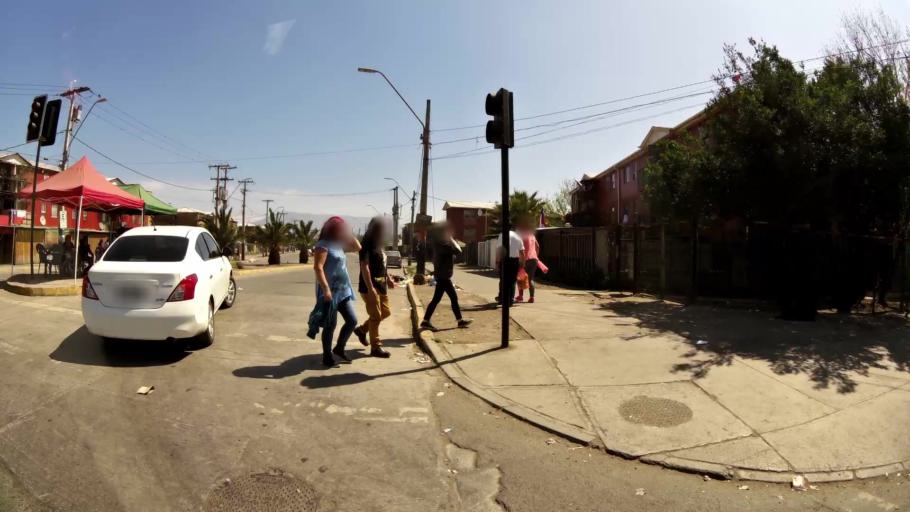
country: CL
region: Santiago Metropolitan
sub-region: Provincia de Santiago
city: Lo Prado
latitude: -33.4055
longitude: -70.7456
